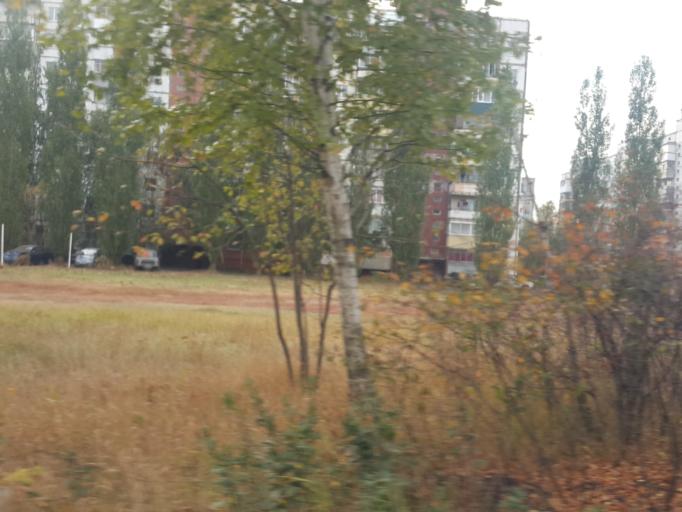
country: RU
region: Tambov
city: Pokrovo-Prigorodnoye
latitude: 52.6827
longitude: 41.4571
